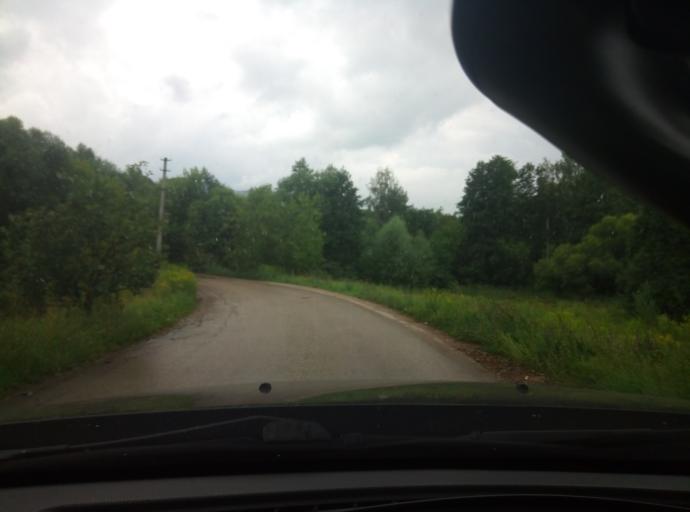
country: RU
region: Tula
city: Lomintsevskiy
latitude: 53.9582
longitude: 37.6434
